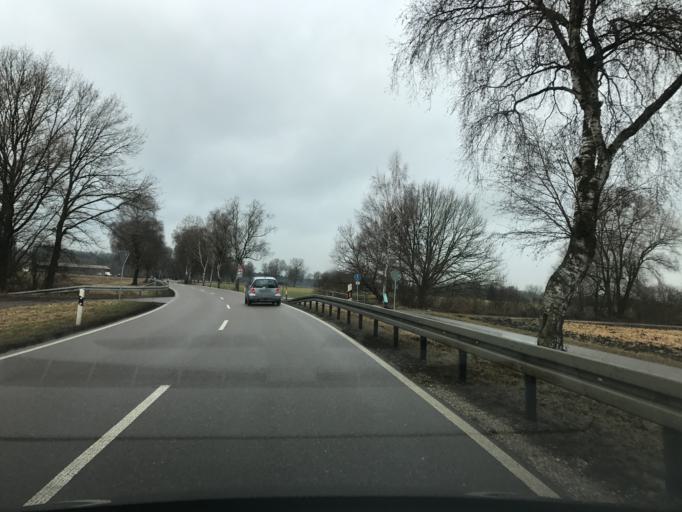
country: DE
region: Baden-Wuerttemberg
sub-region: Tuebingen Region
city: Ersingen
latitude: 48.2559
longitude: 9.8485
